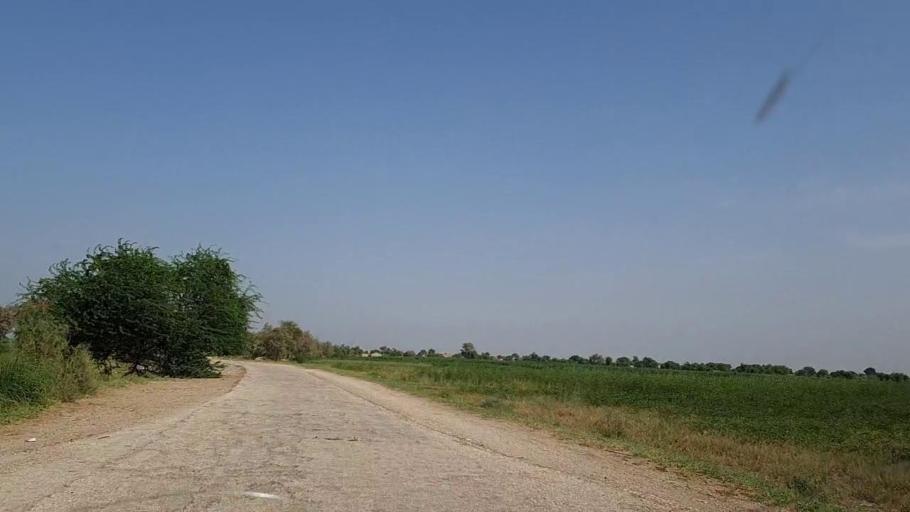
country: PK
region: Sindh
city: Khanpur
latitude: 27.7335
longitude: 69.3546
